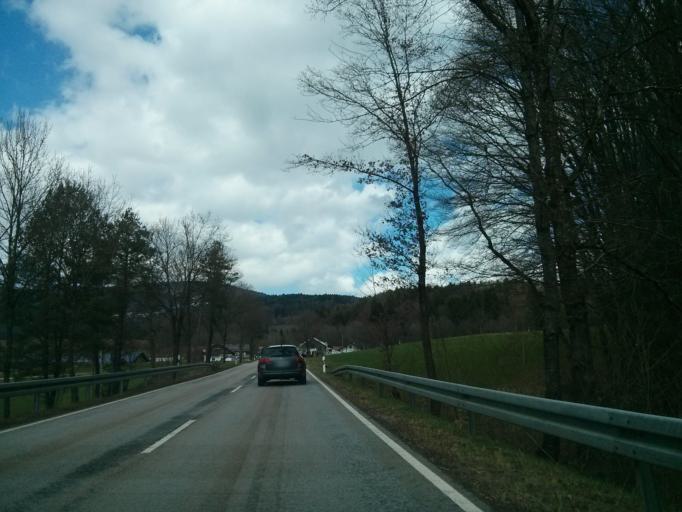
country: DE
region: Bavaria
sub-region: Lower Bavaria
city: Schaufling
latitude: 48.8430
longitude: 13.0879
